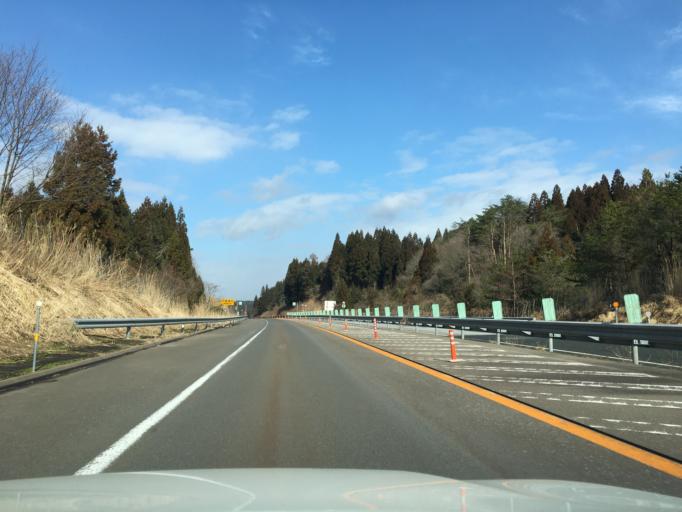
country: JP
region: Akita
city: Akita
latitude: 39.7291
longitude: 140.1796
